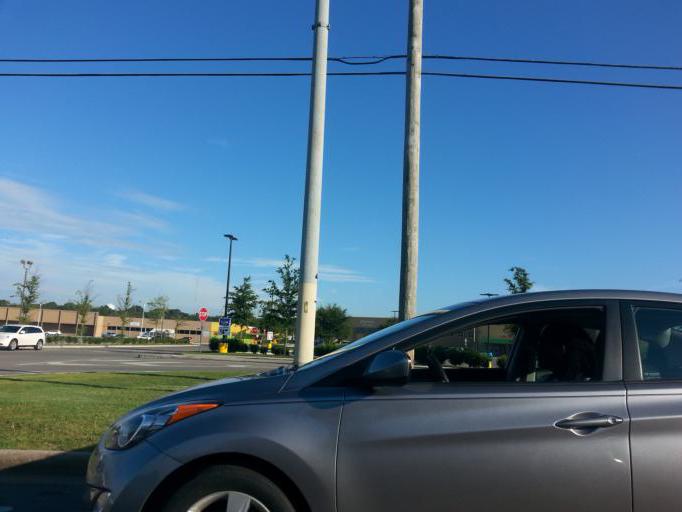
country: US
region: Alabama
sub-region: Lauderdale County
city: East Florence
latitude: 34.8192
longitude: -87.6569
